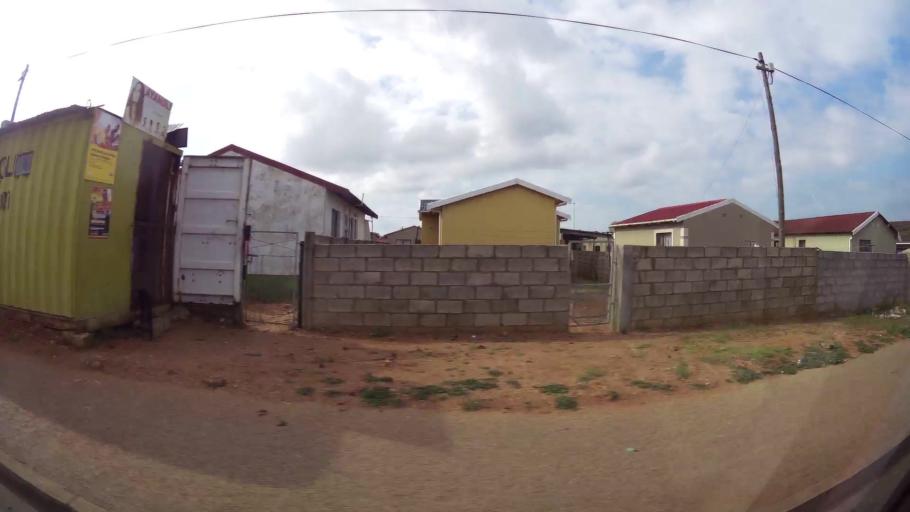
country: ZA
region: Eastern Cape
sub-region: Nelson Mandela Bay Metropolitan Municipality
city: Port Elizabeth
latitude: -33.8176
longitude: 25.5842
